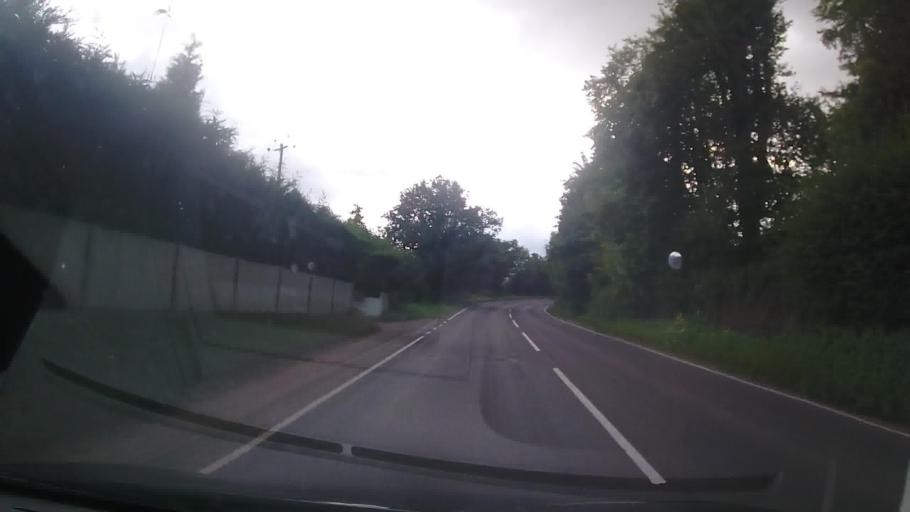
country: GB
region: England
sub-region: Shropshire
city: Great Hanwood
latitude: 52.6963
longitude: -2.7885
